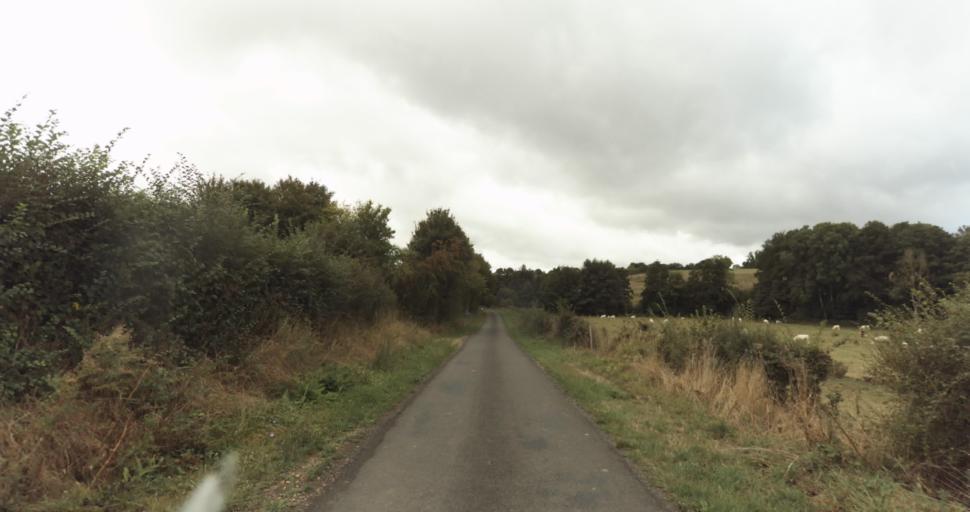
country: FR
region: Lower Normandy
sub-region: Departement de l'Orne
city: Gace
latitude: 48.8648
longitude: 0.2846
